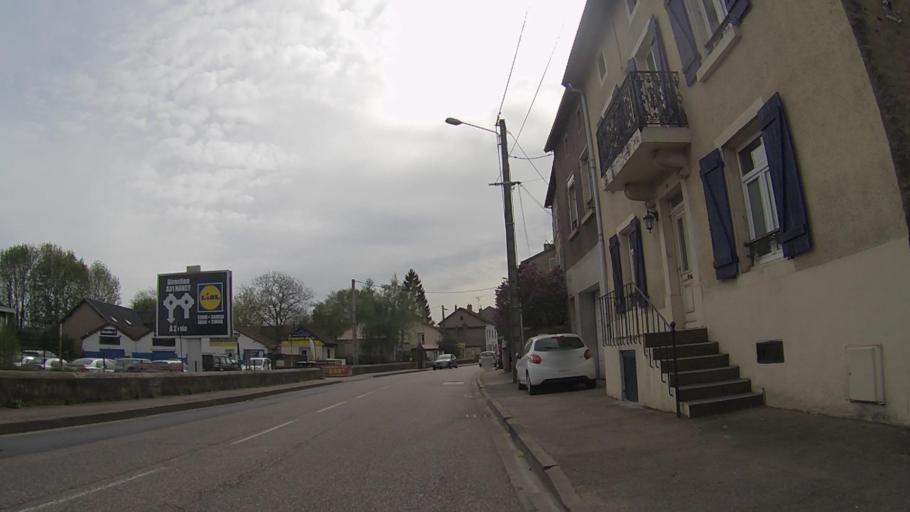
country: FR
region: Lorraine
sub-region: Departement de la Moselle
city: Ars-sur-Moselle
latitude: 49.0775
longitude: 6.0805
